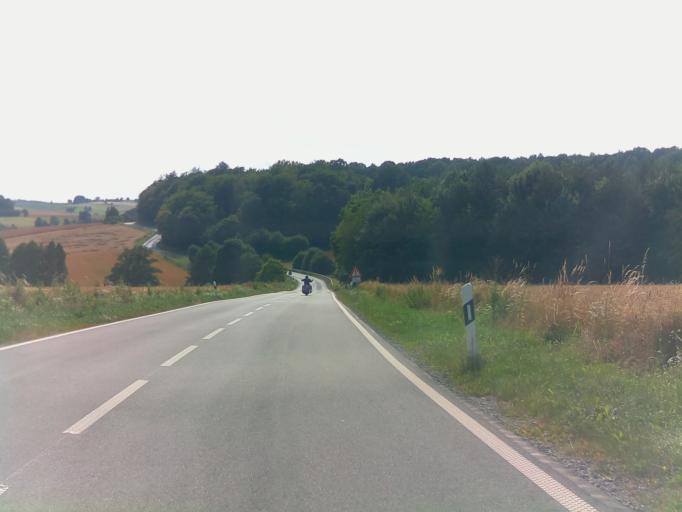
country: DE
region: Baden-Wuerttemberg
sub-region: Regierungsbezirk Stuttgart
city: Buch am Ahorn
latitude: 49.5362
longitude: 9.5289
